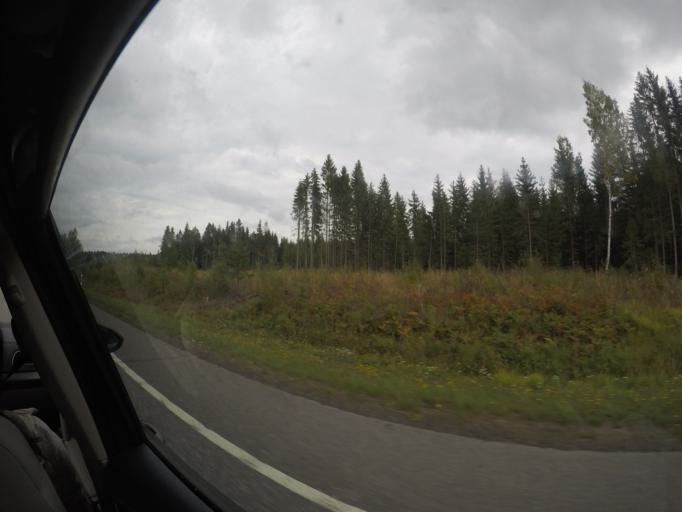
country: FI
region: Haeme
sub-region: Haemeenlinna
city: Parola
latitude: 61.1772
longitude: 24.4123
